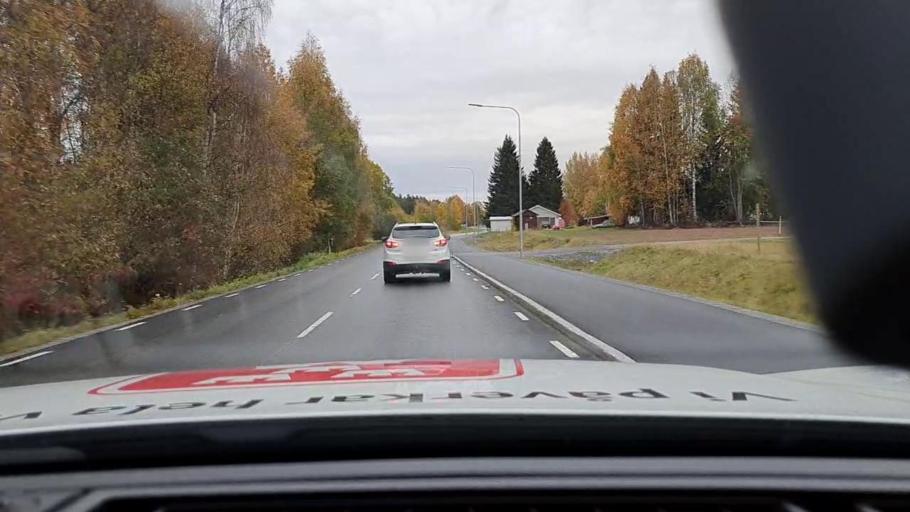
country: SE
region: Norrbotten
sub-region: Bodens Kommun
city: Saevast
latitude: 65.7729
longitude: 21.6987
